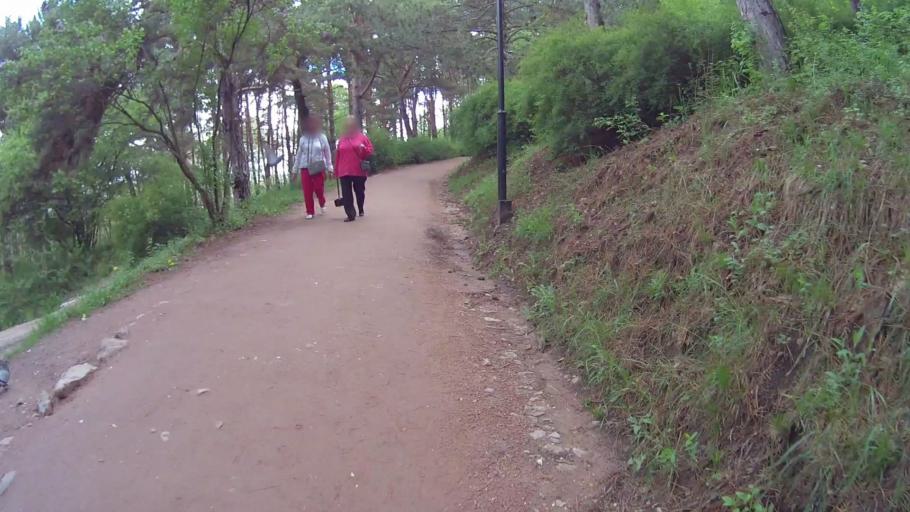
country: RU
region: Stavropol'skiy
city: Kislovodsk
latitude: 43.8996
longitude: 42.7478
